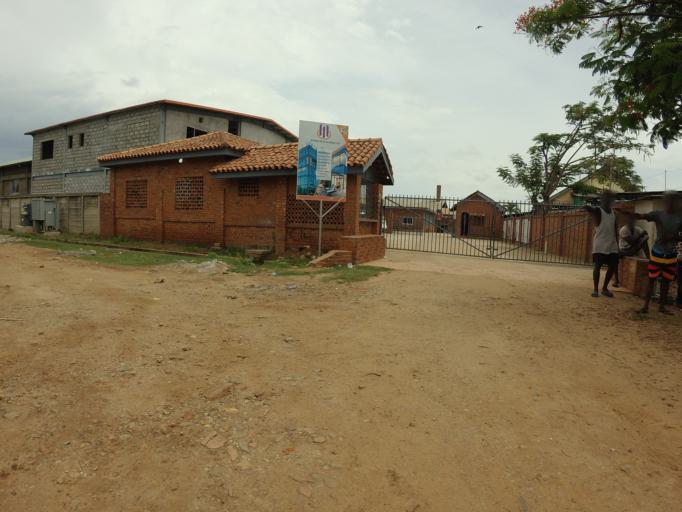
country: GH
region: Greater Accra
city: Accra
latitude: 5.6035
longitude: -0.2122
